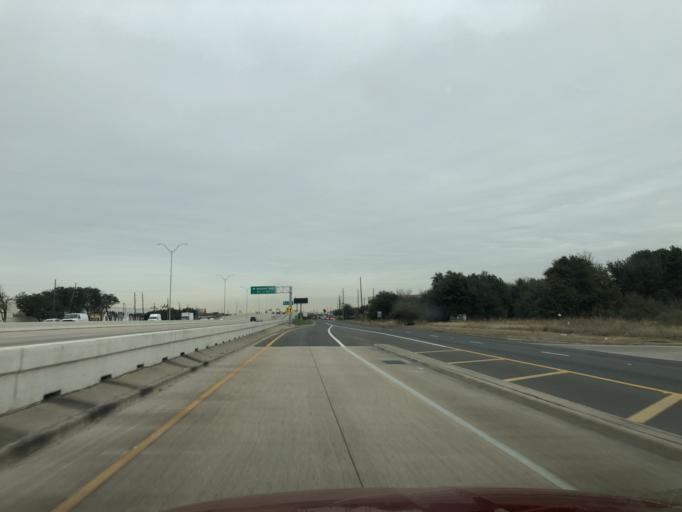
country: US
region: Texas
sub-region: Fort Bend County
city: Missouri City
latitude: 29.6405
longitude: -95.5345
